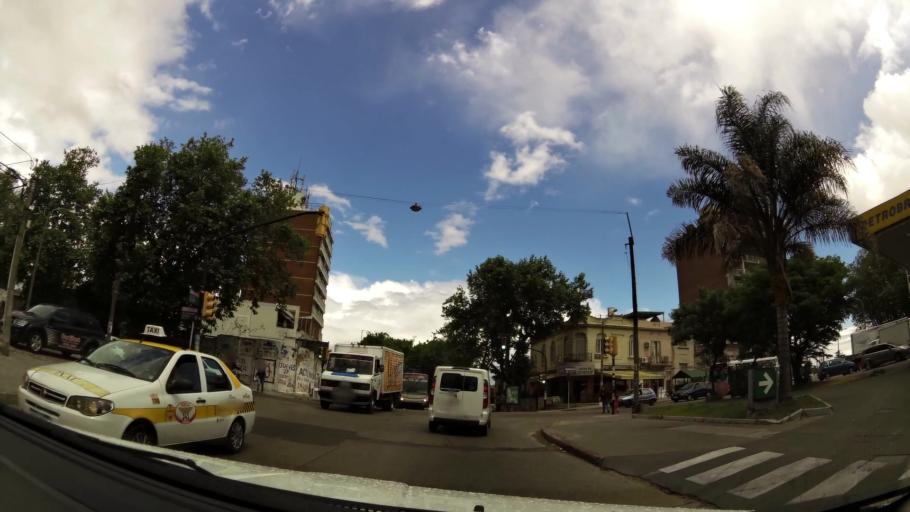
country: UY
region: Montevideo
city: Montevideo
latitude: -34.8628
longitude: -56.1790
